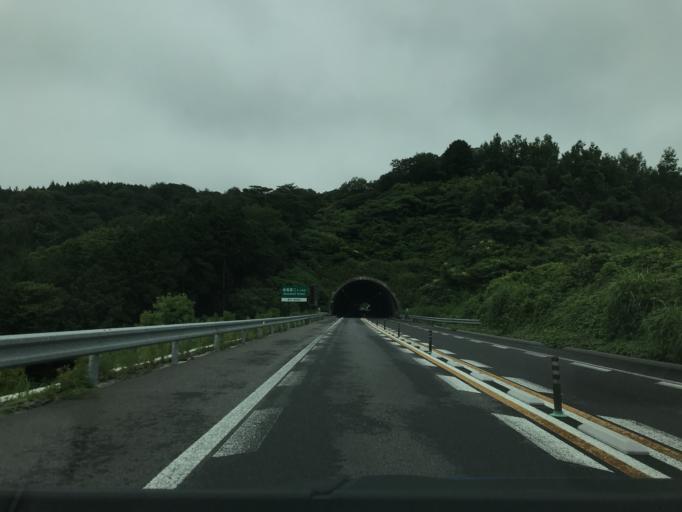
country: JP
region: Fukuoka
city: Nakatsu
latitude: 33.5146
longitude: 131.2782
